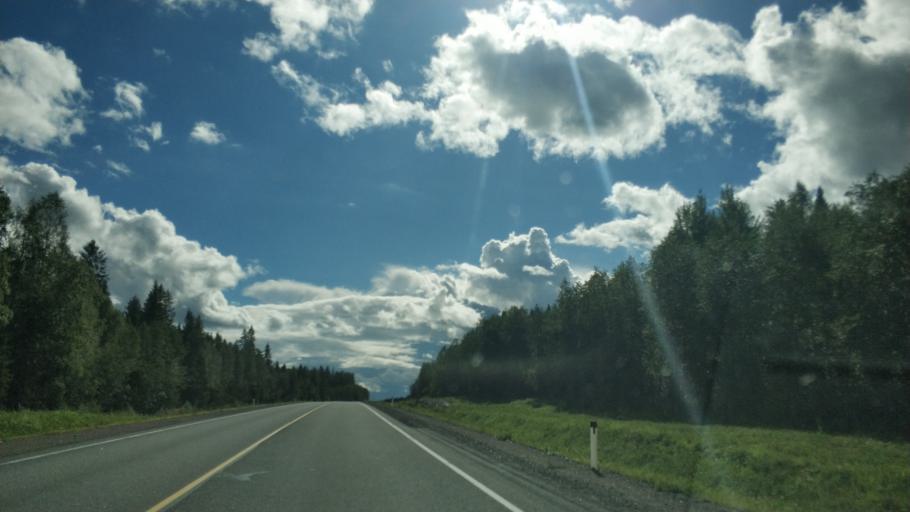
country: RU
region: Republic of Karelia
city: Ruskeala
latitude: 61.8667
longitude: 30.6541
